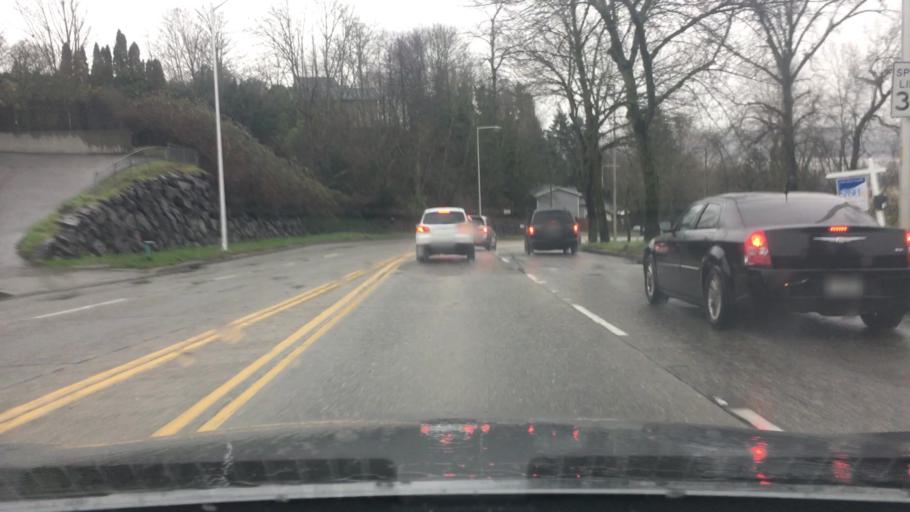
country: US
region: Washington
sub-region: King County
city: White Center
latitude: 47.5188
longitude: -122.3393
